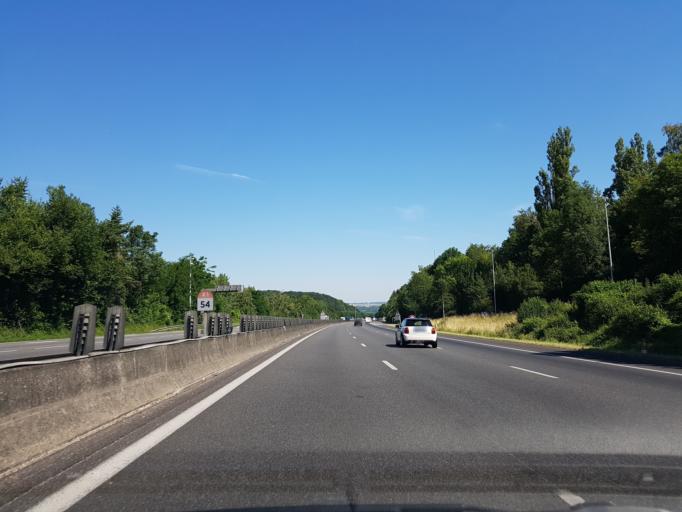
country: FR
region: Picardie
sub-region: Departement de l'Oise
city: Pontpoint
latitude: 49.2877
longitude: 2.6924
